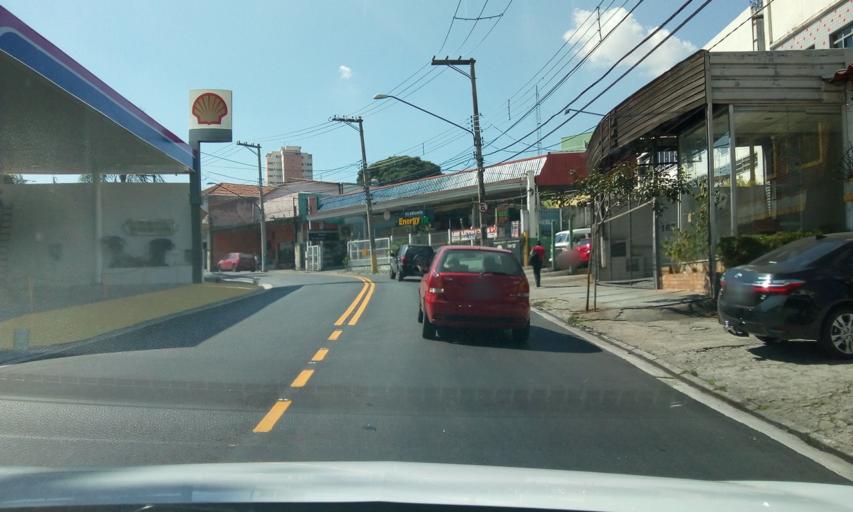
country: BR
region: Sao Paulo
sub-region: Sao Paulo
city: Sao Paulo
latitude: -23.4972
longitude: -46.5987
